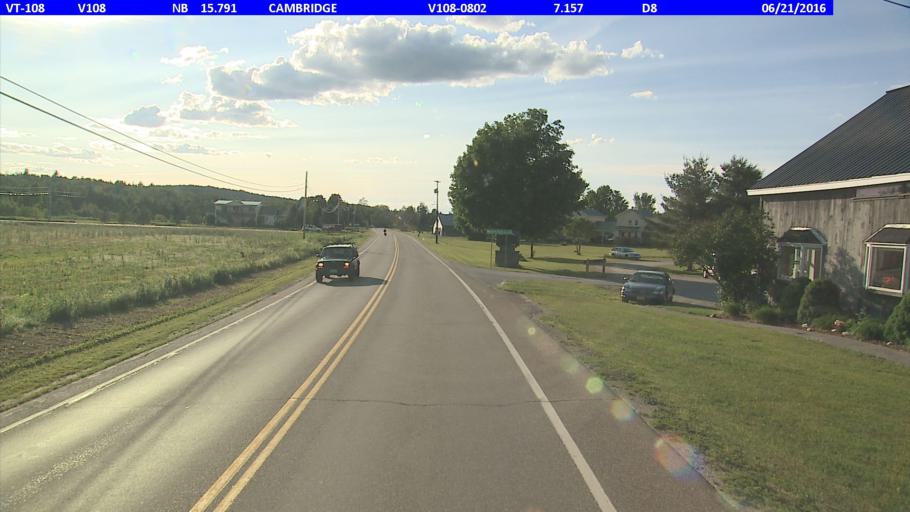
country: US
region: Vermont
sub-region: Lamoille County
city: Johnson
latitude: 44.6238
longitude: -72.8258
